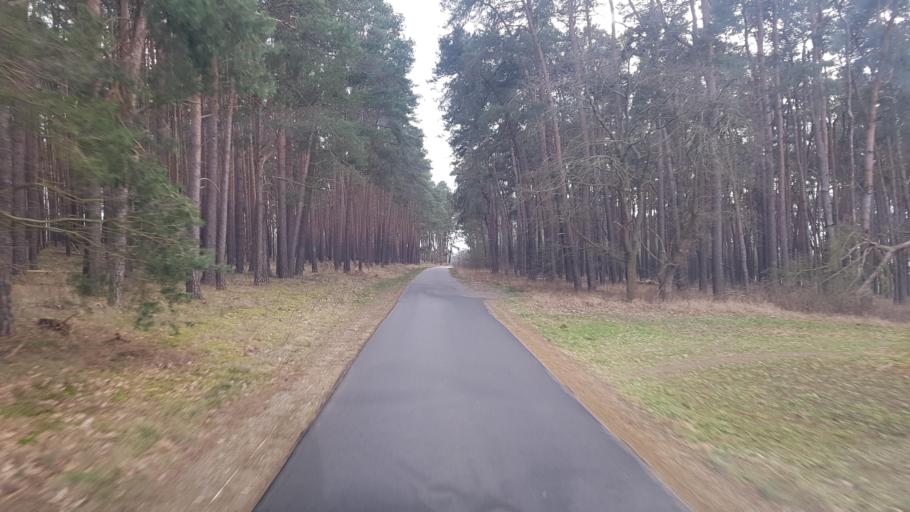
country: DE
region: Brandenburg
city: Drahnsdorf
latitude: 51.9358
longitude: 13.6173
